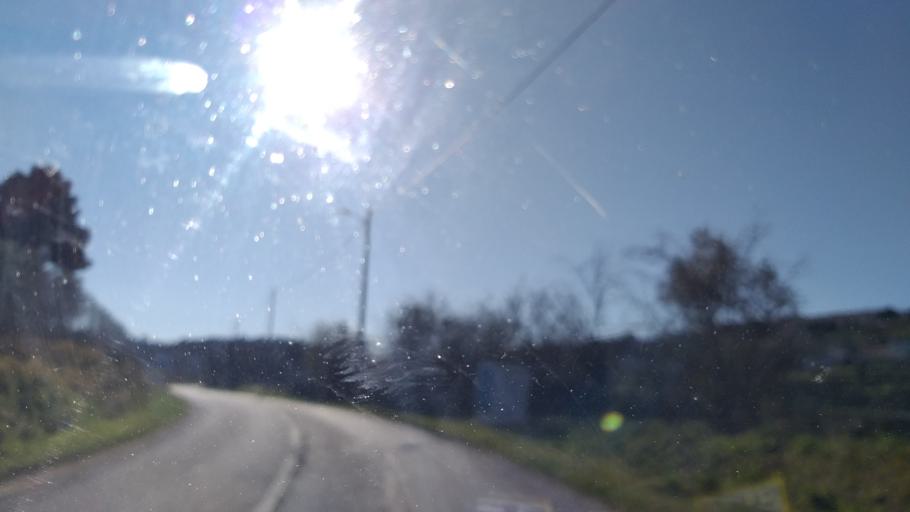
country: PT
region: Guarda
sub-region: Celorico da Beira
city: Celorico da Beira
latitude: 40.6319
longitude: -7.3845
